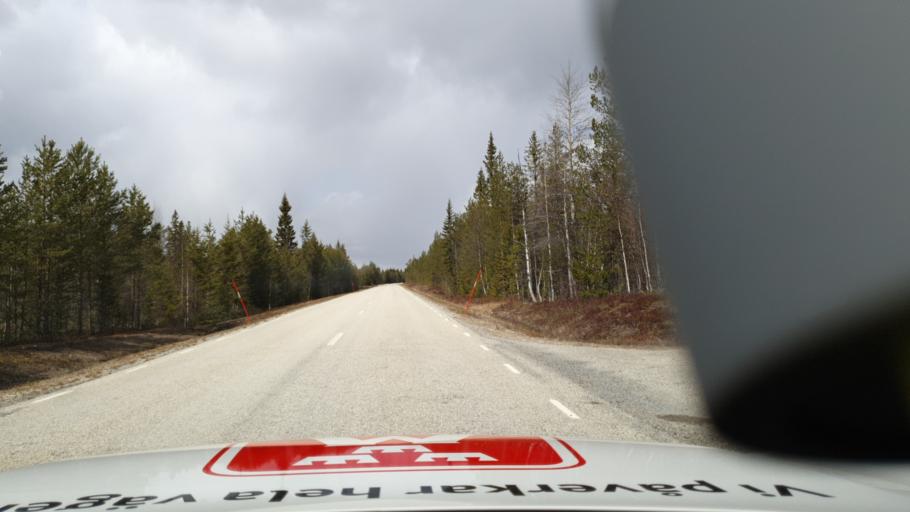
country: SE
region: Jaemtland
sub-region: Are Kommun
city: Jarpen
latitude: 62.7511
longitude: 13.7512
